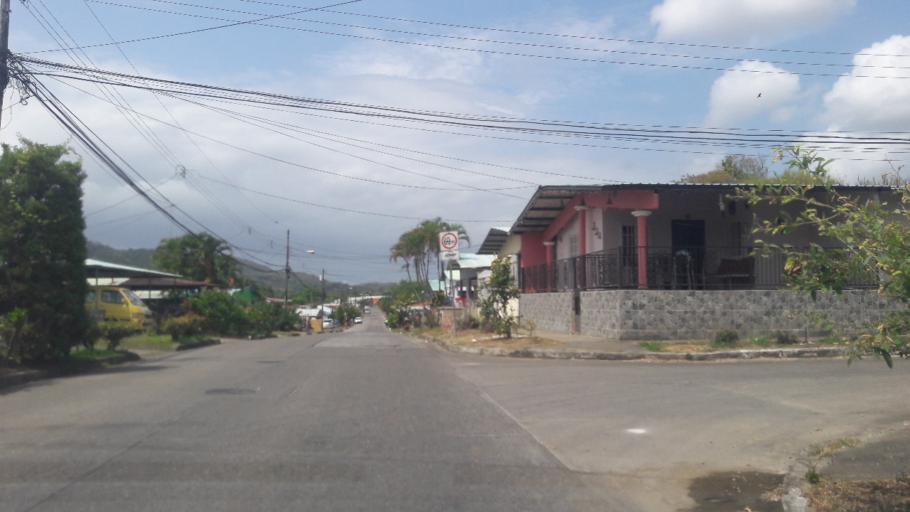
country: PA
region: Panama
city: Alcalde Diaz
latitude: 9.1382
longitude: -79.5507
